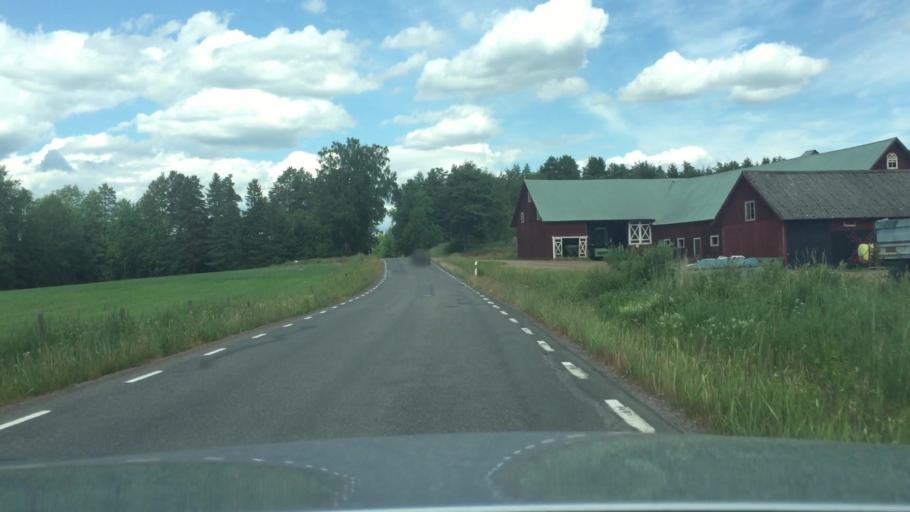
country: SE
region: Vaestra Goetaland
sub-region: Tidaholms Kommun
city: Tidaholm
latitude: 58.2084
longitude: 13.9837
